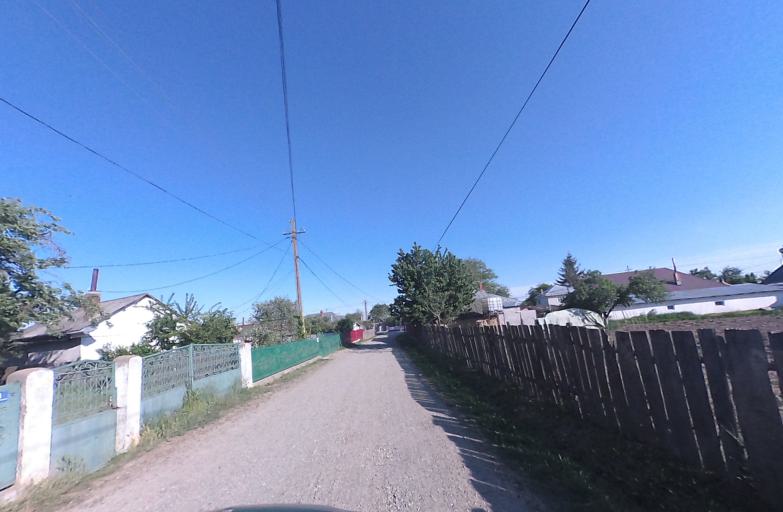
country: RO
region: Neamt
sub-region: Comuna Cordun
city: Pildesti
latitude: 46.9804
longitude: 26.8069
